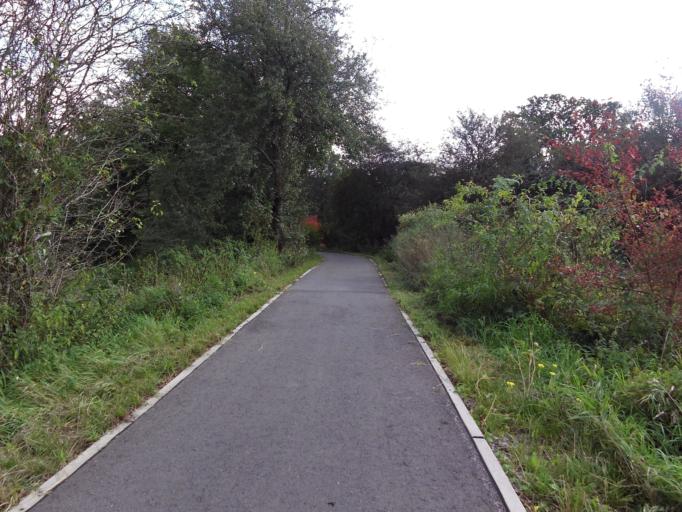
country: DE
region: Saxony-Anhalt
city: Dessau
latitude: 51.8631
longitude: 12.2854
